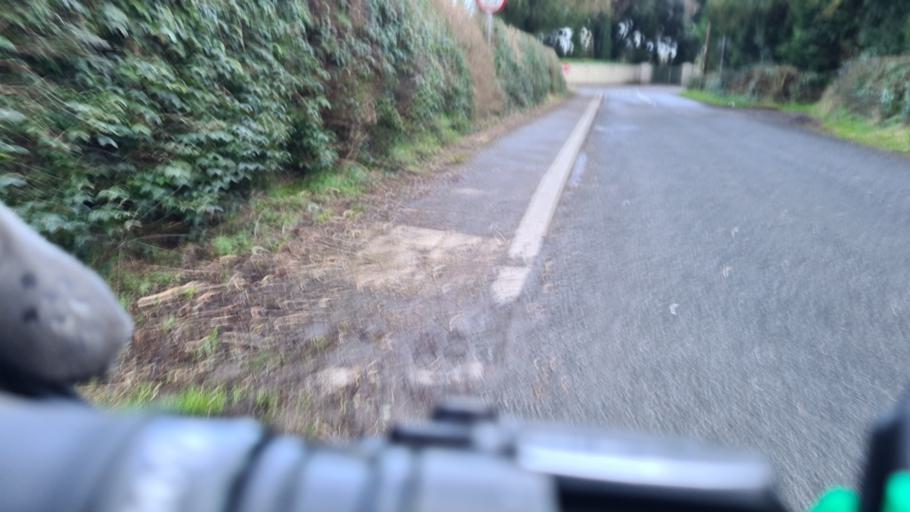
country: IE
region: Leinster
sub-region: Kildare
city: Celbridge
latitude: 53.3330
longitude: -6.5676
